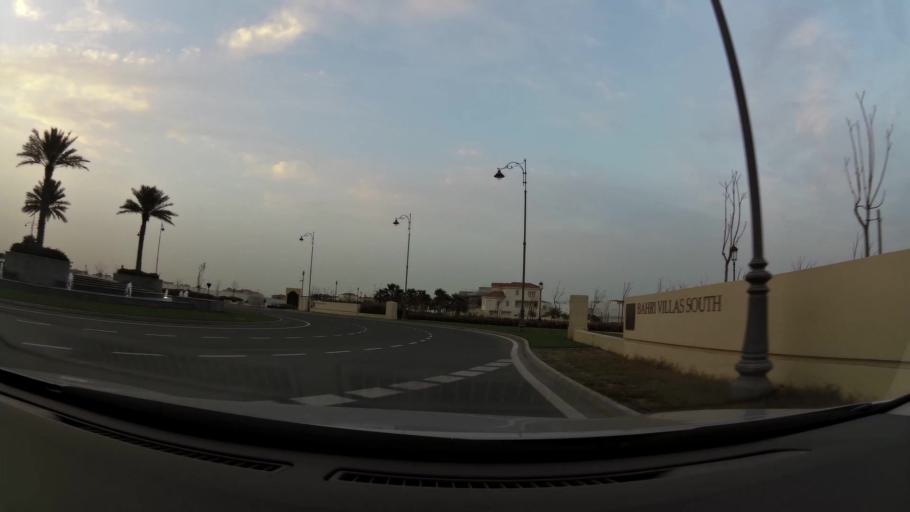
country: QA
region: Baladiyat ad Dawhah
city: Doha
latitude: 25.3694
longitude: 51.5623
